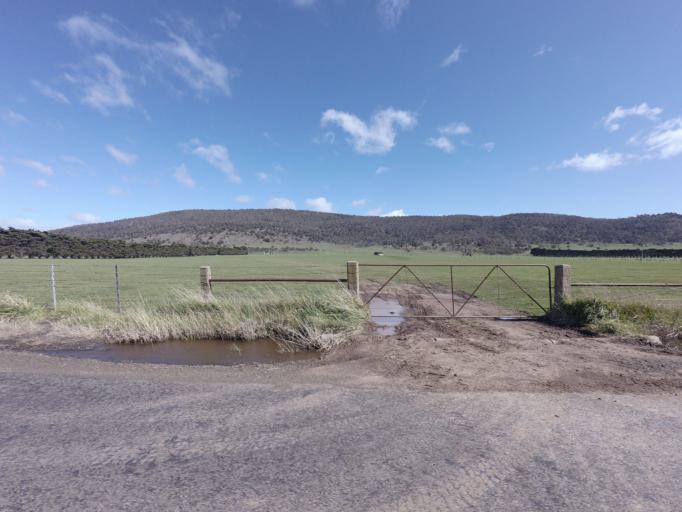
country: AU
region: Tasmania
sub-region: Northern Midlands
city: Evandale
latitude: -41.9650
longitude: 147.4405
